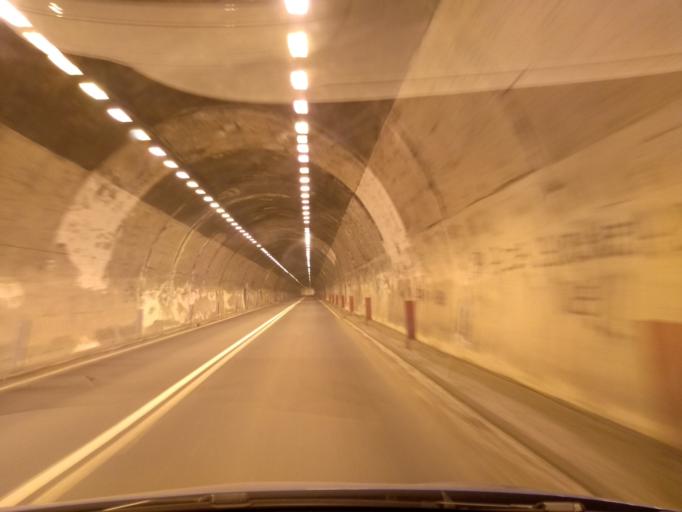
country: IT
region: Piedmont
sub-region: Provincia di Torino
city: Lanzo Torinese
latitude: 45.2656
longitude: 7.4806
